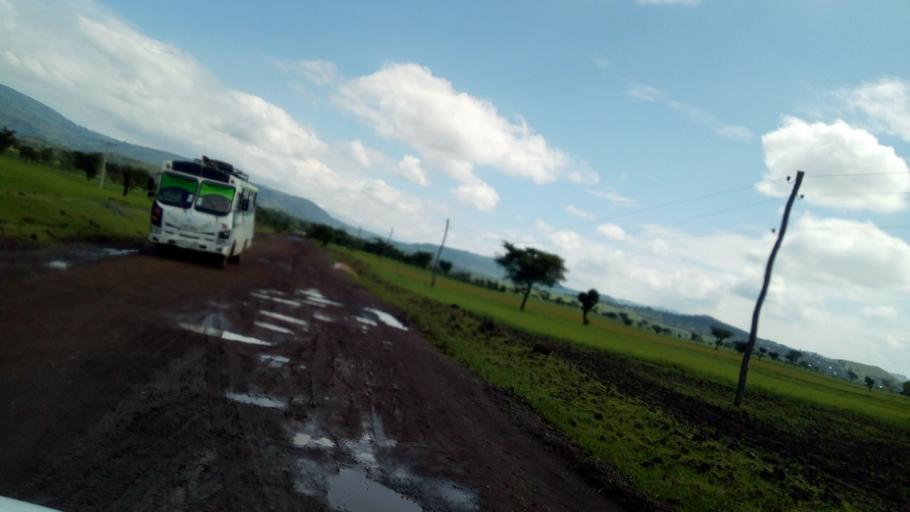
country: ET
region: Oromiya
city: Bishoftu
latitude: 8.8121
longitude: 39.0046
